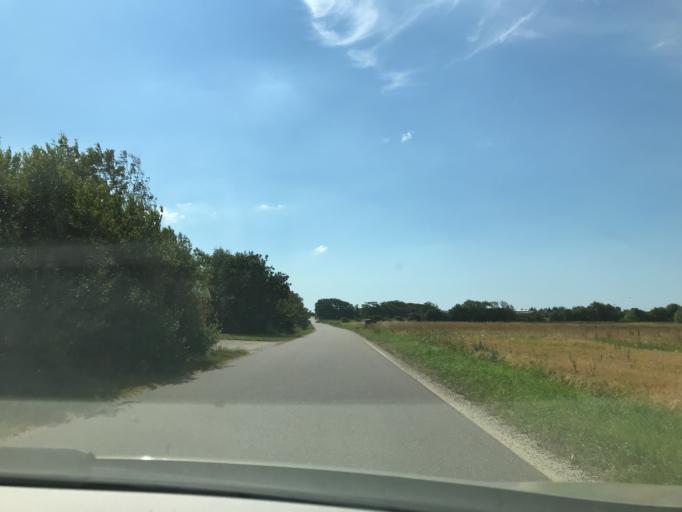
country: DK
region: Central Jutland
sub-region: Ringkobing-Skjern Kommune
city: Skjern
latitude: 55.8898
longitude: 8.4010
